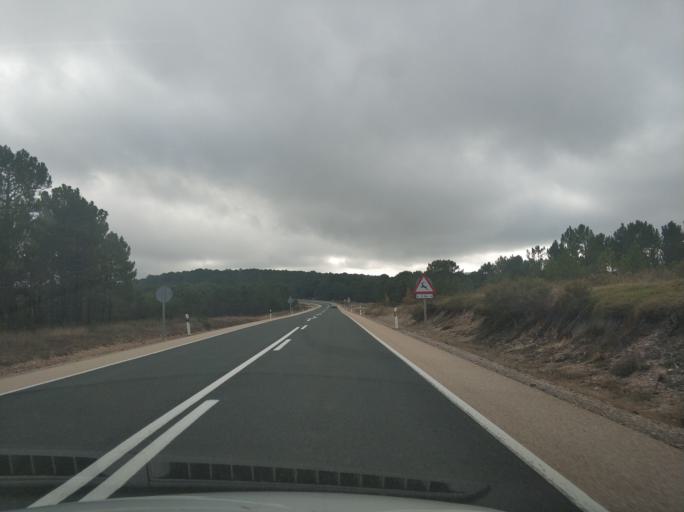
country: ES
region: Castille and Leon
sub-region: Provincia de Soria
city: Muriel Viejo
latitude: 41.8194
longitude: -2.9369
